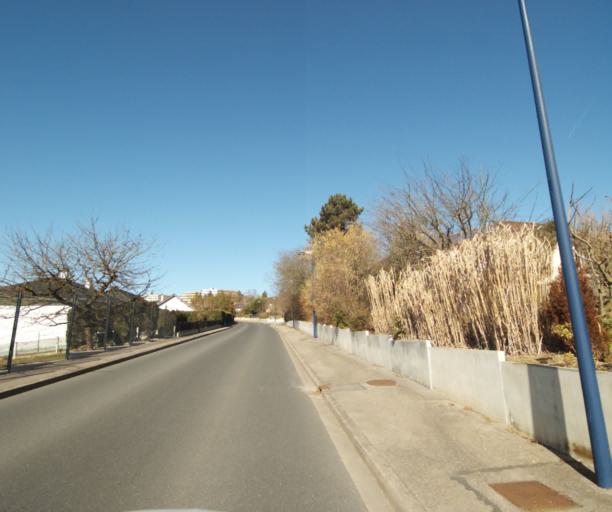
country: FR
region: Lorraine
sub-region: Departement de Meurthe-et-Moselle
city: Ludres
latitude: 48.6126
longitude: 6.1701
